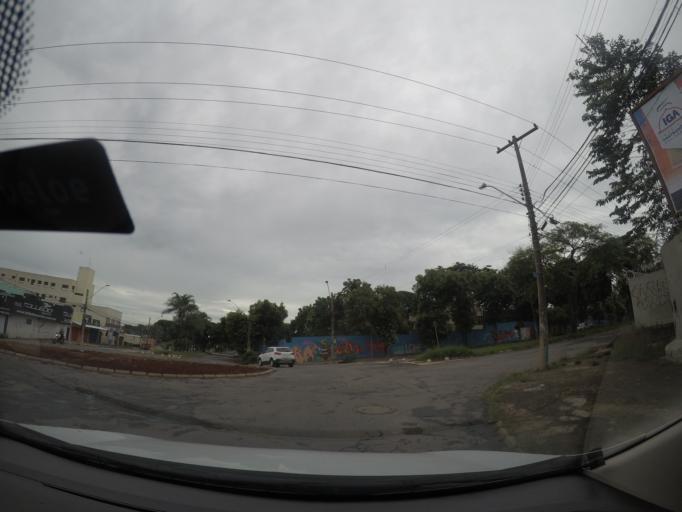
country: BR
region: Goias
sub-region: Goiania
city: Goiania
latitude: -16.6806
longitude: -49.2437
